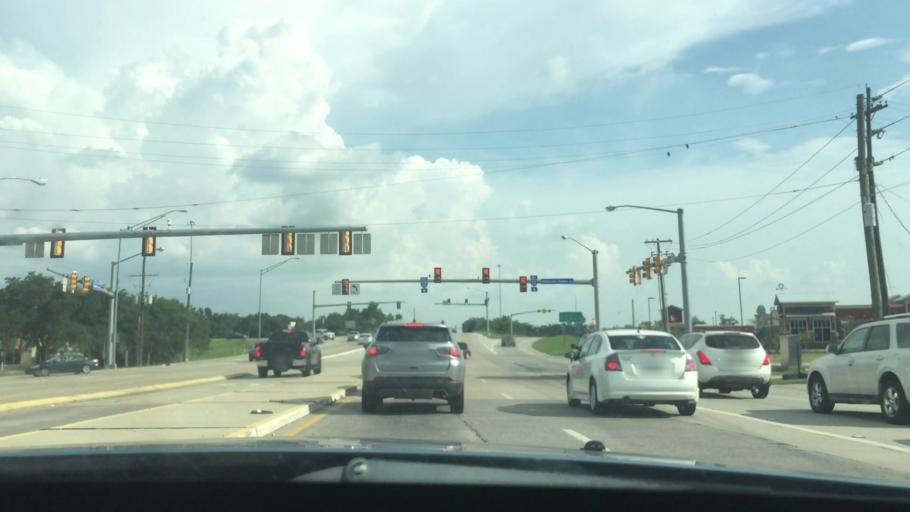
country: US
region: Louisiana
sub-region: East Baton Rouge Parish
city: Shenandoah
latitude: 30.4414
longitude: -91.0244
